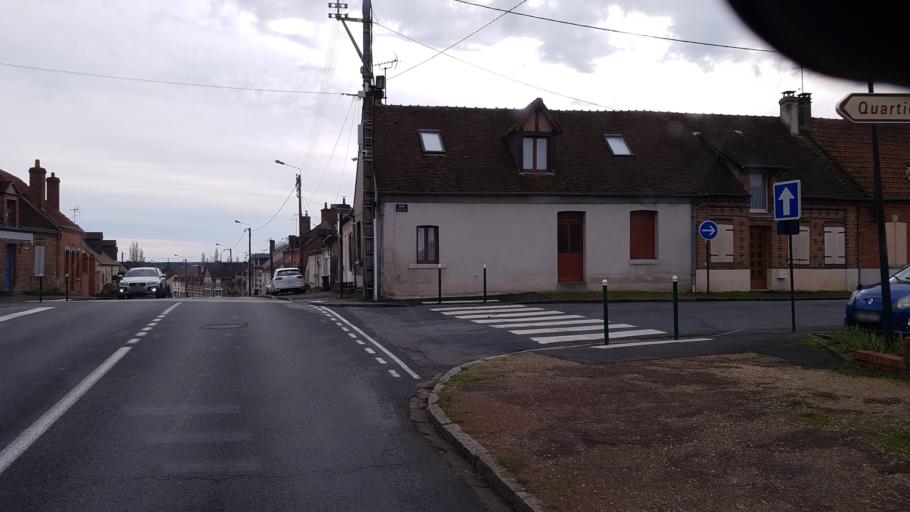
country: FR
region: Centre
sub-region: Departement du Loiret
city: La Ferte-Saint-Aubin
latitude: 47.7107
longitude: 1.9410
